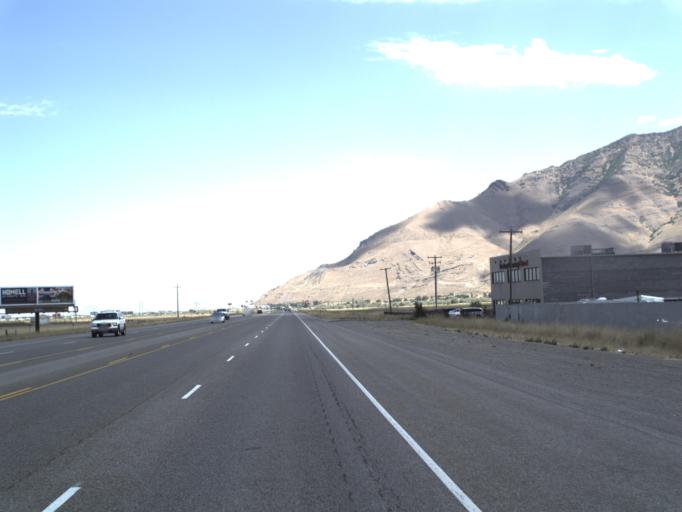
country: US
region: Utah
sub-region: Tooele County
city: Stansbury park
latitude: 40.6669
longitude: -112.2849
